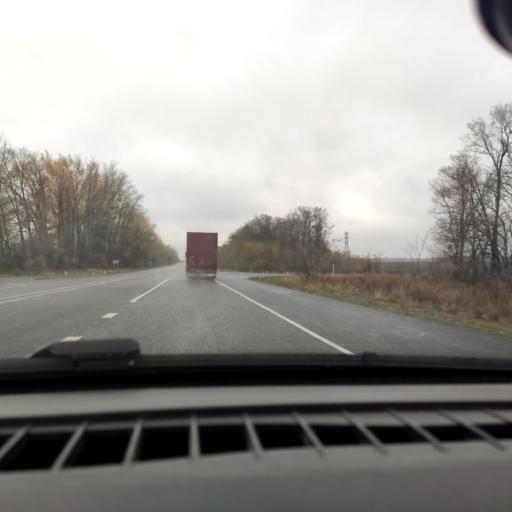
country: RU
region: Voronezj
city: Kolodeznyy
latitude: 51.2560
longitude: 39.0532
